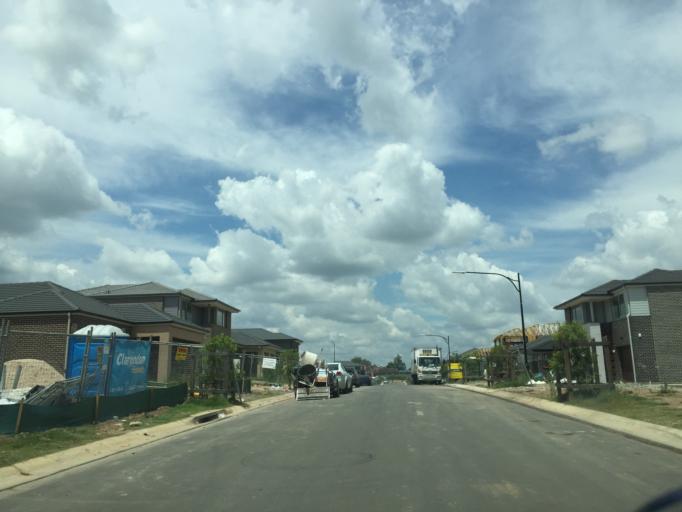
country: AU
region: New South Wales
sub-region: Blacktown
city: Quakers Hill
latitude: -33.7059
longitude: 150.8856
